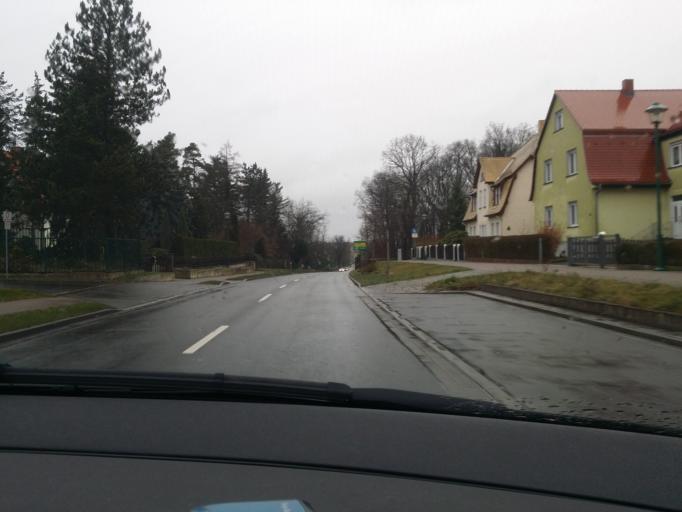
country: DE
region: Saxony
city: Bad Duben
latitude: 51.5971
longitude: 12.5799
